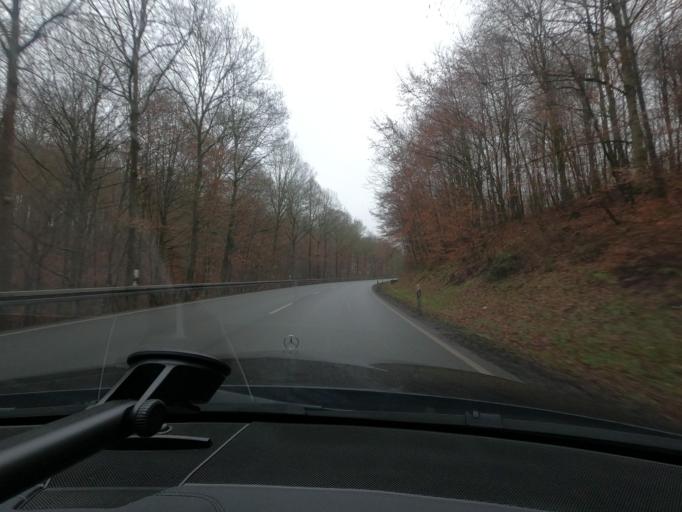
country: DE
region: Hesse
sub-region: Regierungsbezirk Kassel
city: Bad Arolsen
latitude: 51.3558
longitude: 9.0660
